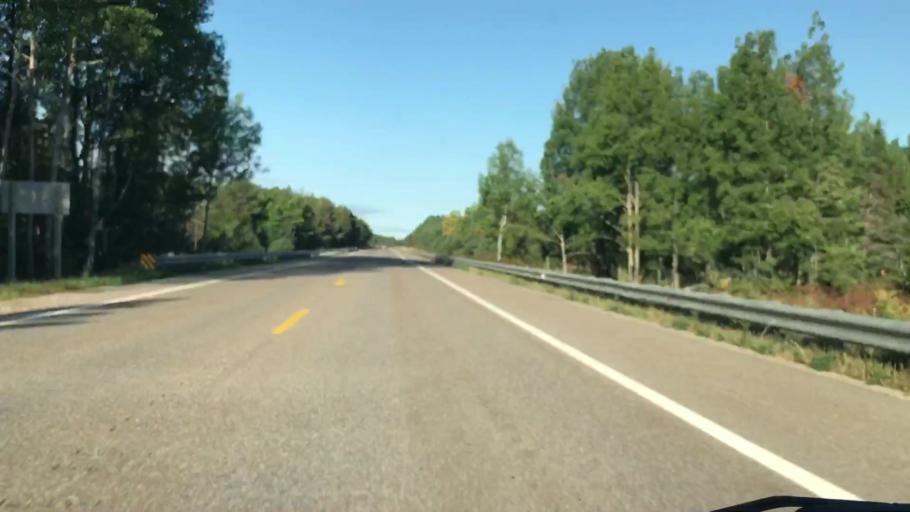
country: US
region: Michigan
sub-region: Mackinac County
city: Saint Ignace
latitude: 46.3584
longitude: -84.8646
